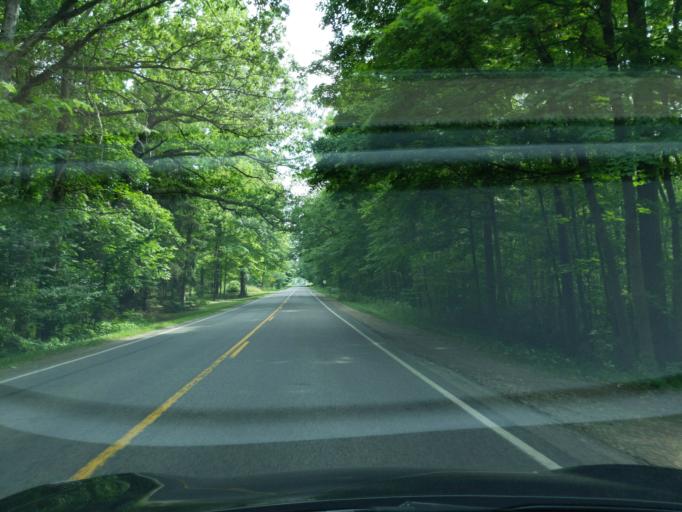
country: US
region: Michigan
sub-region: Eaton County
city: Dimondale
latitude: 42.6340
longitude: -84.6029
